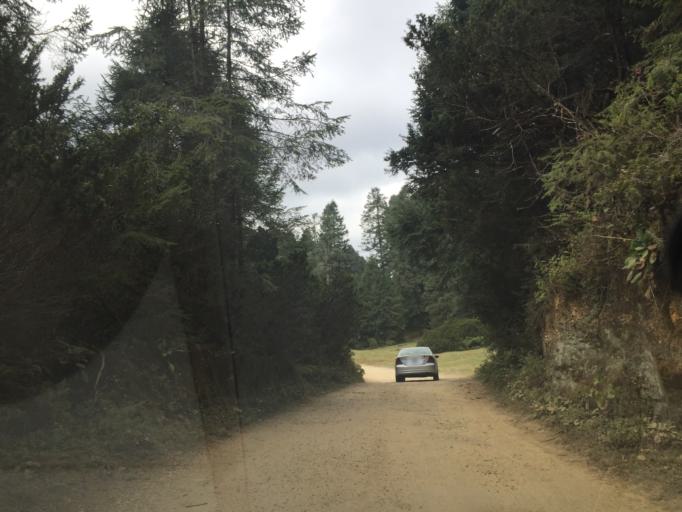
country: MX
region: Michoacan
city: Mineral de Angangueo
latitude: 19.6623
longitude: -100.2717
